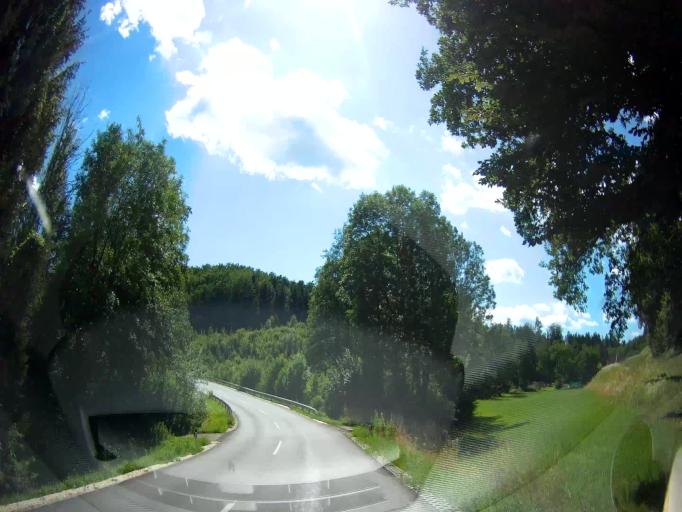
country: AT
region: Carinthia
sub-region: Politischer Bezirk Volkermarkt
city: Voelkermarkt
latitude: 46.6516
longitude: 14.5498
